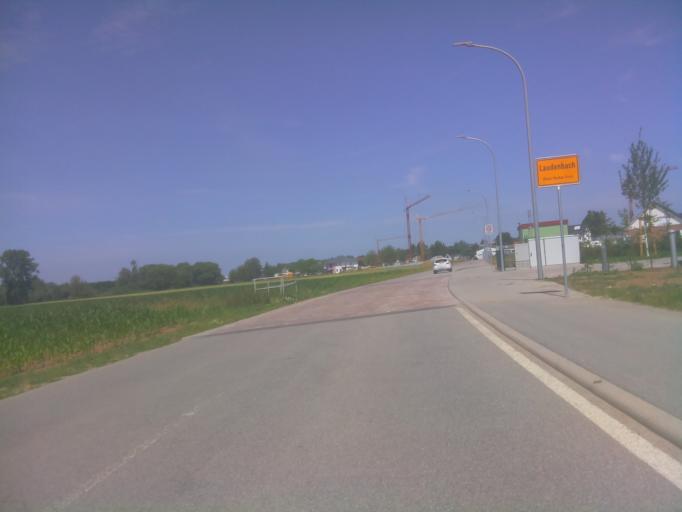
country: DE
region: Baden-Wuerttemberg
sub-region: Karlsruhe Region
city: Laudenbach
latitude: 49.6066
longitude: 8.6430
